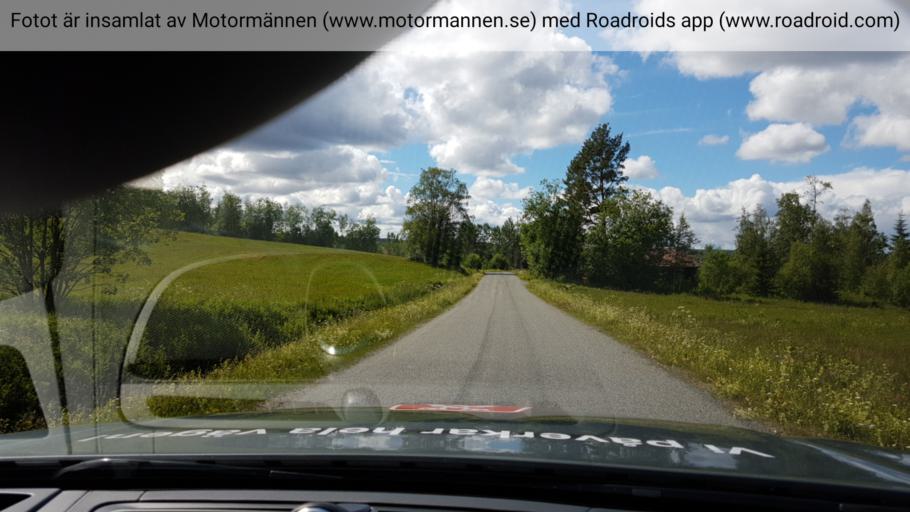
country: SE
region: Jaemtland
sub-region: Bergs Kommun
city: Hoverberg
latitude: 62.8482
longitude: 14.4222
